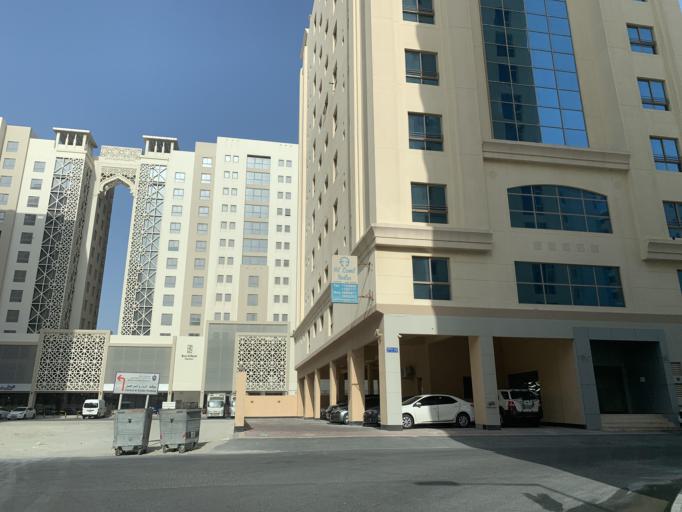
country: BH
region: Muharraq
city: Al Muharraq
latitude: 26.2641
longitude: 50.5960
